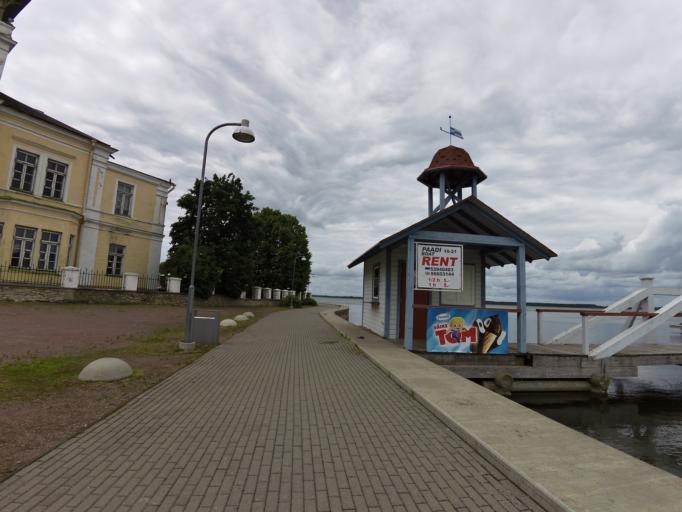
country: EE
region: Laeaene
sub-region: Haapsalu linn
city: Haapsalu
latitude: 58.9514
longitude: 23.5360
